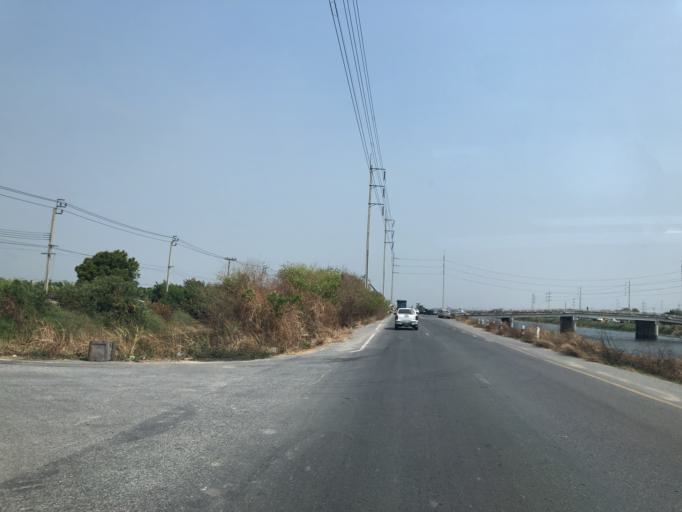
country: TH
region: Samut Prakan
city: Bang Bo District
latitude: 13.5252
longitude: 100.7478
